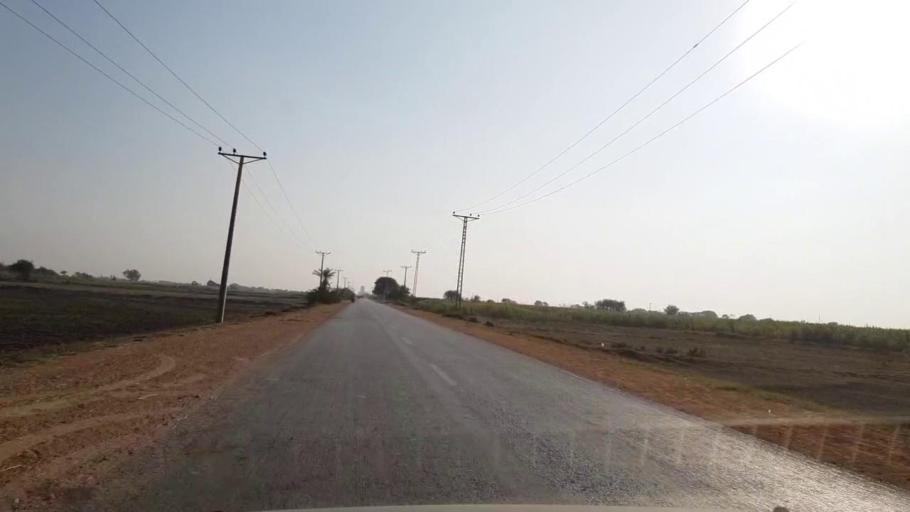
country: PK
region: Sindh
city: Bulri
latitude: 24.8497
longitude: 68.3270
